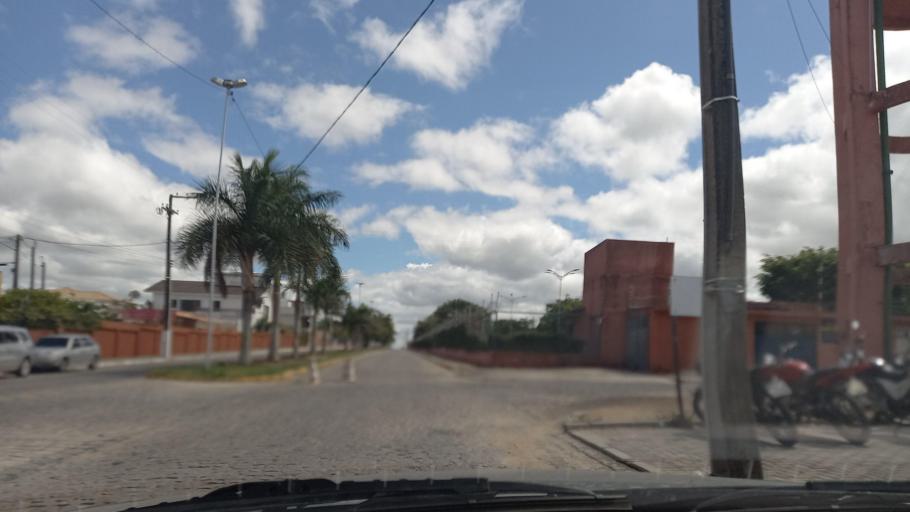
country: BR
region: Pernambuco
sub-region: Caruaru
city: Caruaru
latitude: -8.2502
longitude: -35.9501
